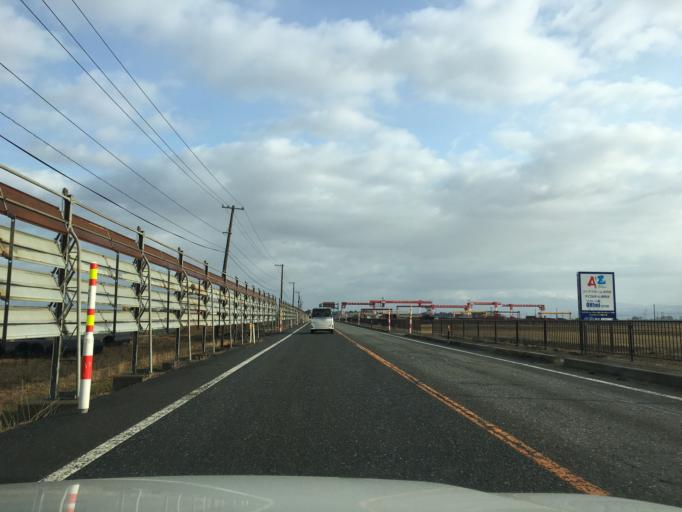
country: JP
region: Yamagata
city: Sakata
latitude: 38.8363
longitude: 139.8479
